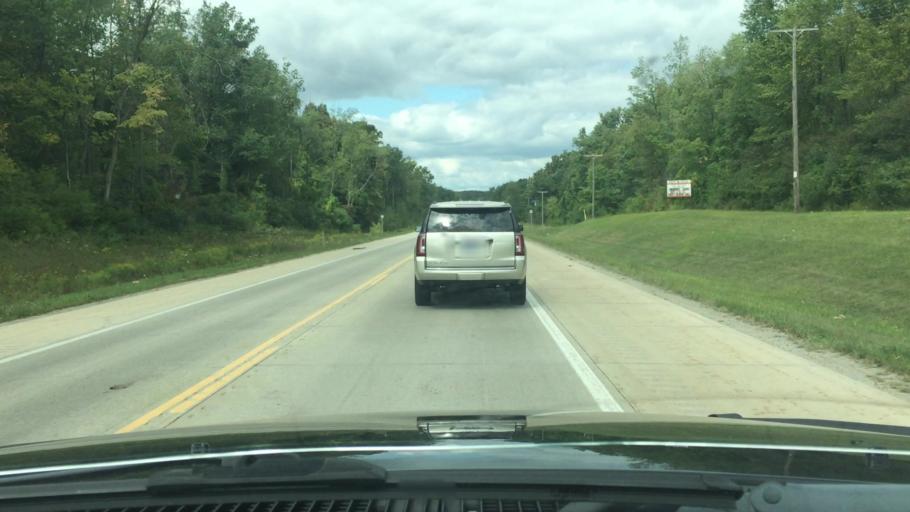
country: US
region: Michigan
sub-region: Lapeer County
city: Almont
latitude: 42.8787
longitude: -83.0305
